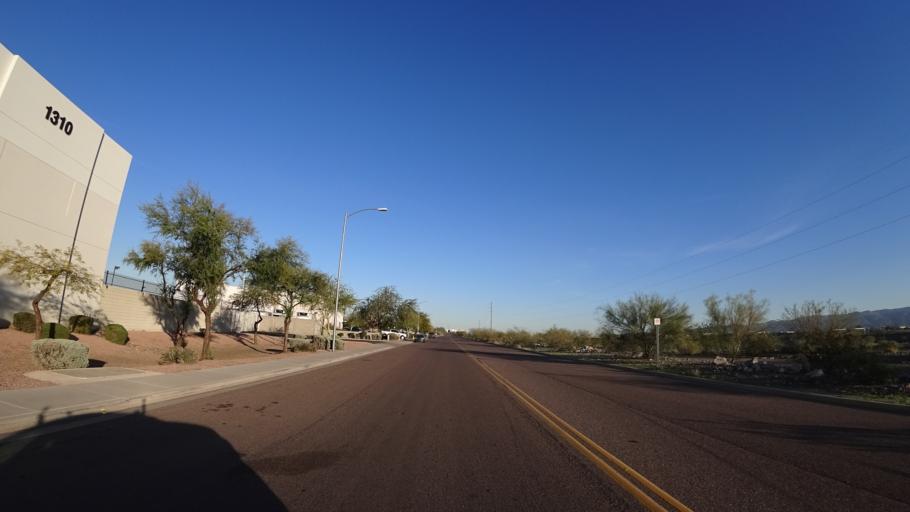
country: US
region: Arizona
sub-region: Maricopa County
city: Phoenix
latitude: 33.4211
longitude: -112.0539
